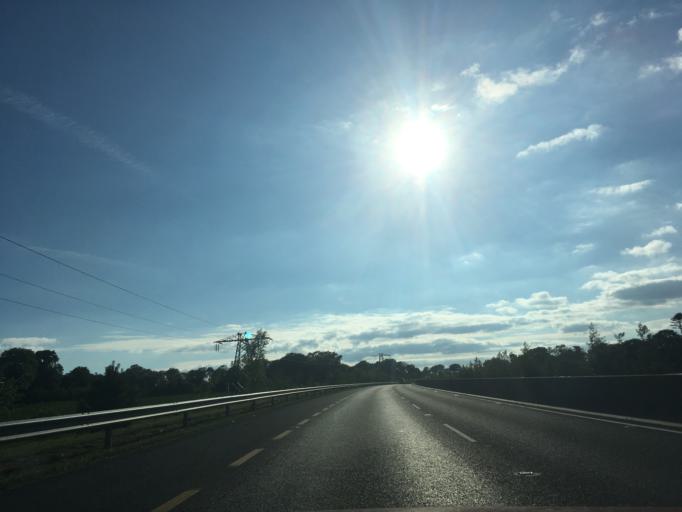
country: IE
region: Munster
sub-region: Waterford
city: Waterford
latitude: 52.2882
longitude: -7.0872
